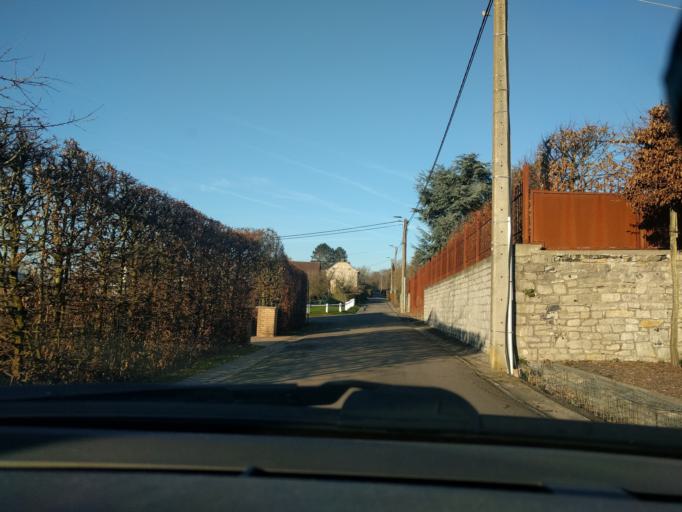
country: BE
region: Wallonia
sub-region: Province de Namur
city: Namur
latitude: 50.4675
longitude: 4.9112
